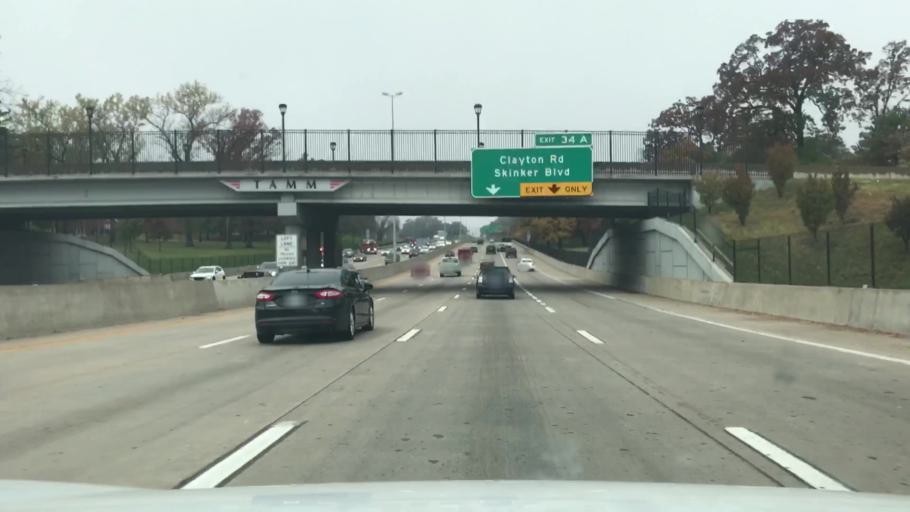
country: US
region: Missouri
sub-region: Saint Louis County
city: Richmond Heights
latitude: 38.6324
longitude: -90.2930
